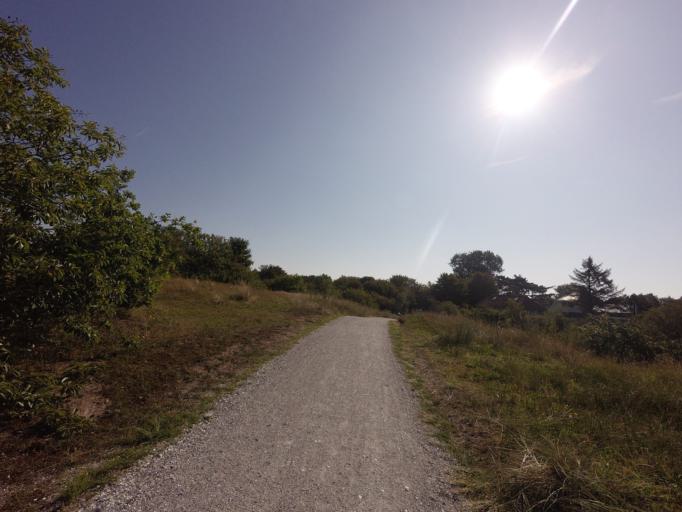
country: NL
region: Friesland
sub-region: Gemeente Schiermonnikoog
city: Schiermonnikoog
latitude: 53.4822
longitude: 6.1653
